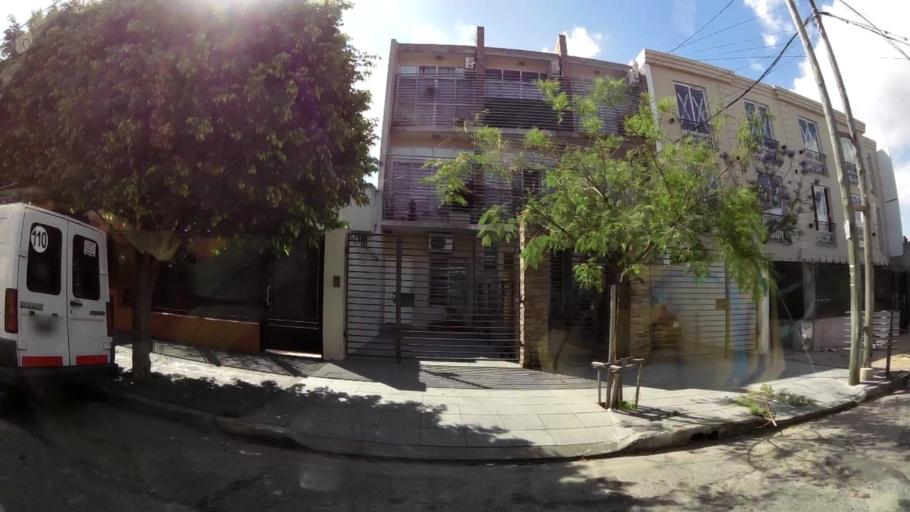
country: AR
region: Buenos Aires
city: San Justo
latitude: -34.6452
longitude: -58.5536
